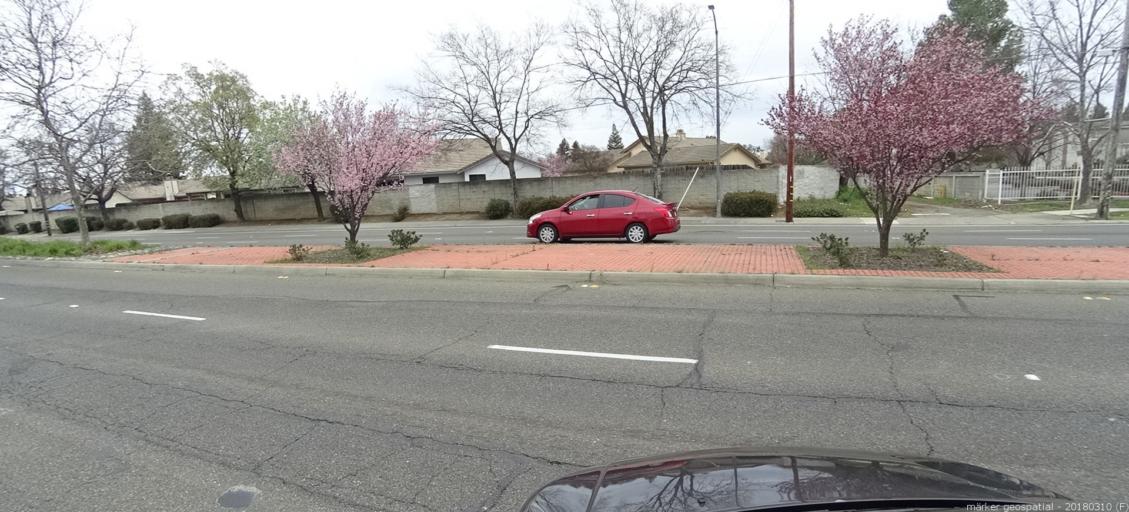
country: US
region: California
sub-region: Sacramento County
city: Vineyard
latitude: 38.4675
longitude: -121.3733
